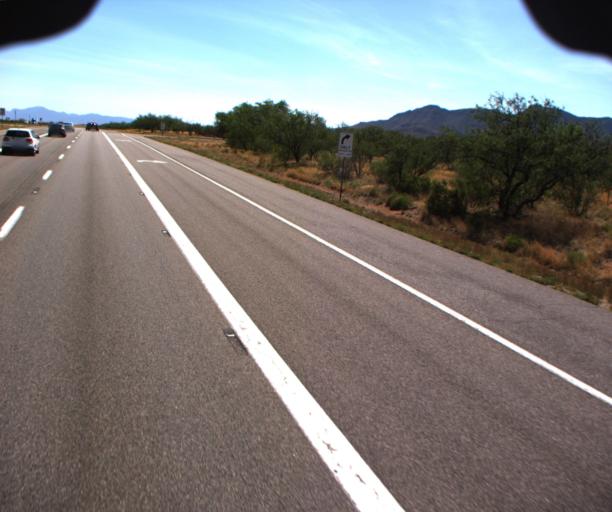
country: US
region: Arizona
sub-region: Cochise County
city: Whetstone
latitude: 31.8369
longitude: -110.3435
